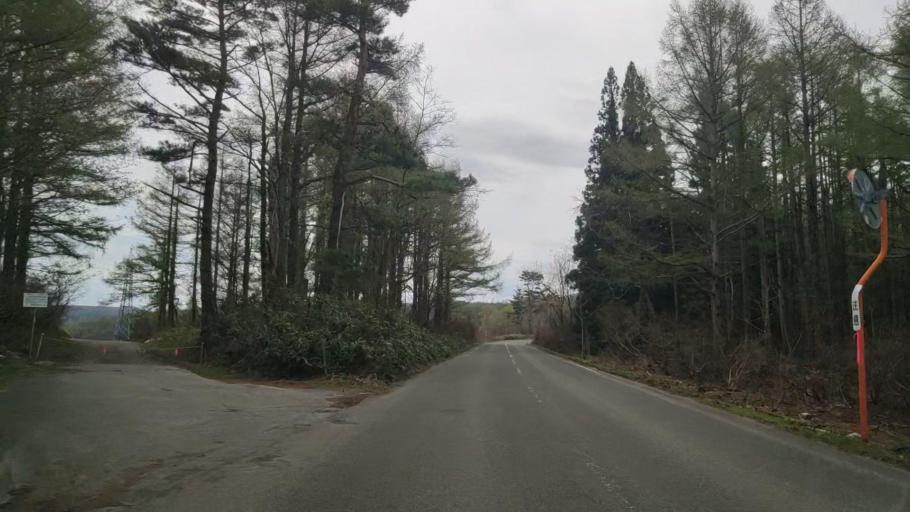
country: JP
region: Aomori
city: Aomori Shi
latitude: 40.7280
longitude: 140.8476
